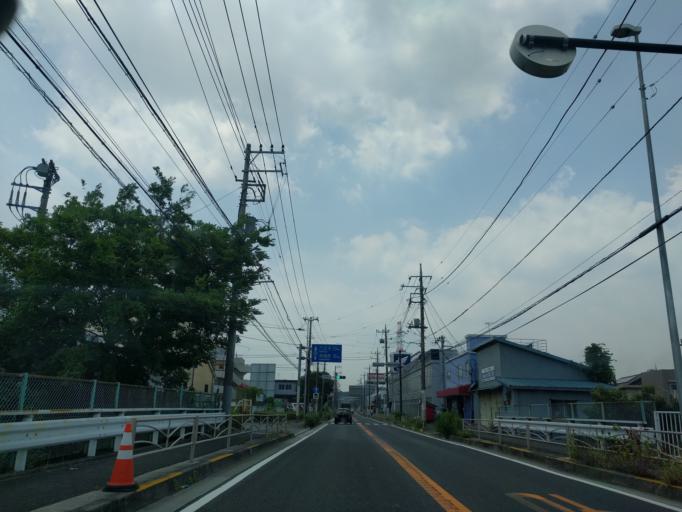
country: JP
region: Kanagawa
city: Minami-rinkan
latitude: 35.4870
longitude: 139.5200
